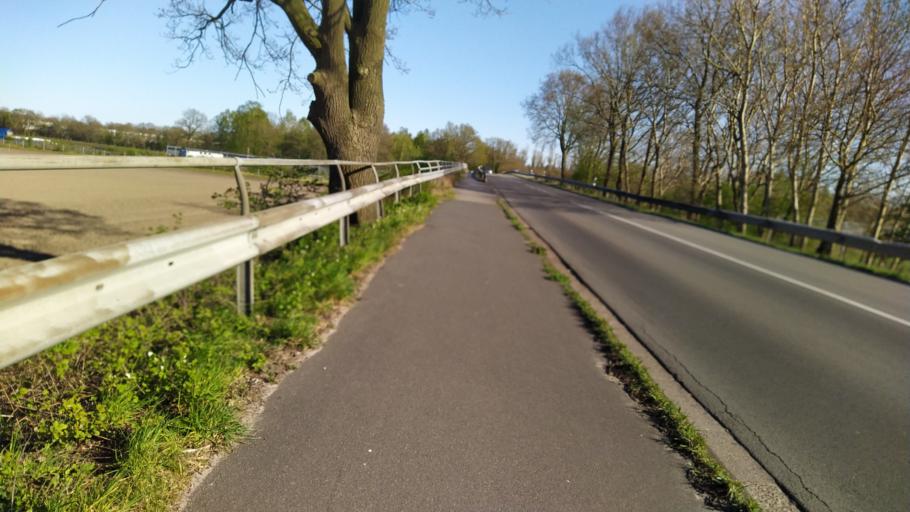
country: DE
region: Lower Saxony
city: Gross Meckelsen
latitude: 53.2837
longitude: 9.4725
